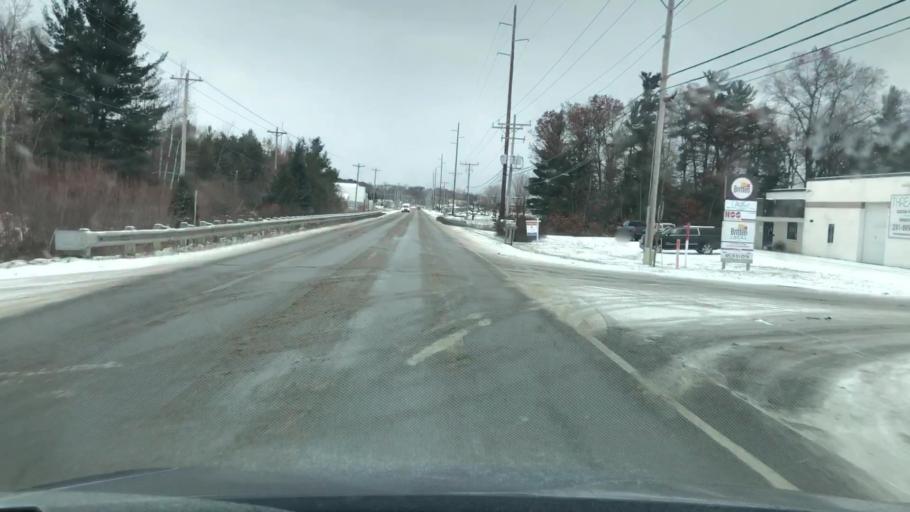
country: US
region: Michigan
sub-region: Grand Traverse County
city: Traverse City
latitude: 44.7218
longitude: -85.6258
